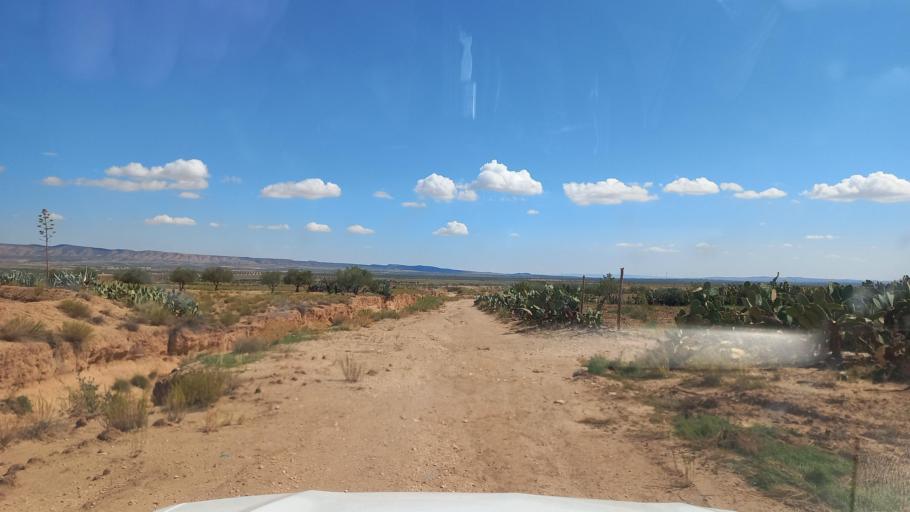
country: TN
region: Al Qasrayn
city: Sbiba
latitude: 35.3550
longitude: 9.0159
